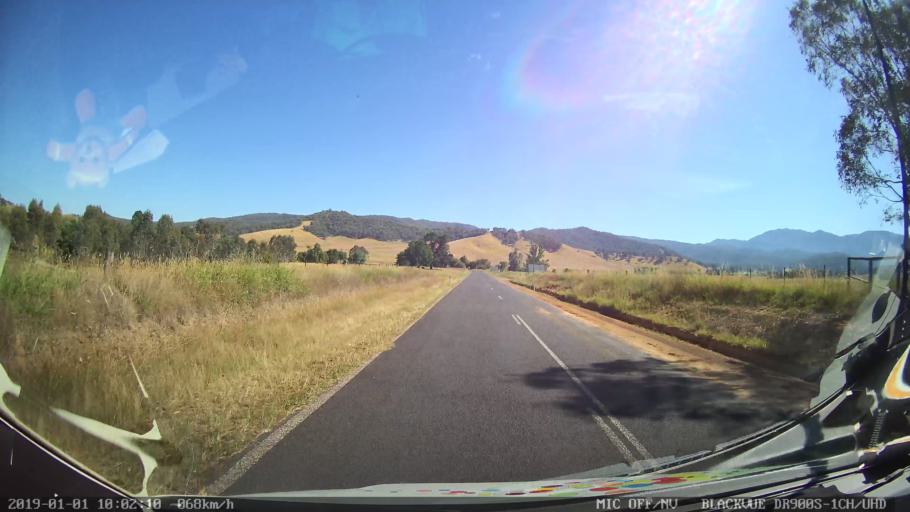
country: AU
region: New South Wales
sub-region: Snowy River
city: Jindabyne
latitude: -36.1839
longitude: 148.1016
